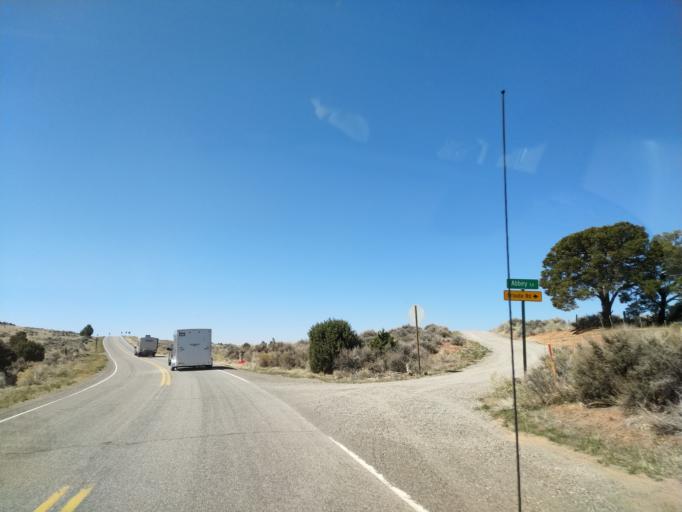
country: US
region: Colorado
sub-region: Mesa County
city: Redlands
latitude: 39.0047
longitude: -108.7048
